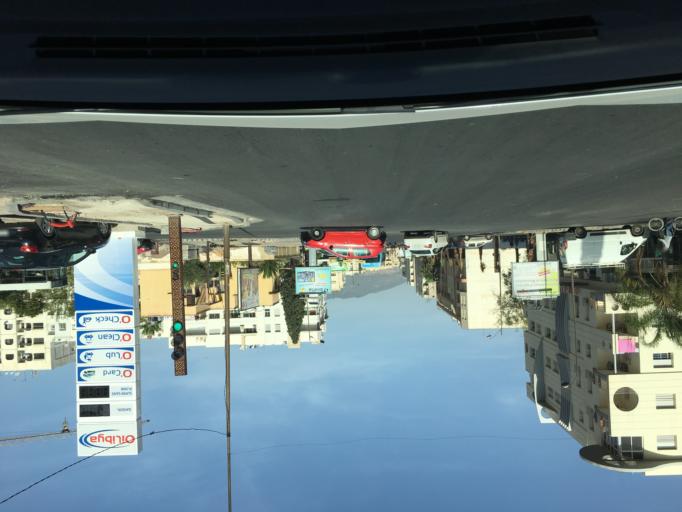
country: MA
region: Fes-Boulemane
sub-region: Fes
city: Fes
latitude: 34.0389
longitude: -5.0065
